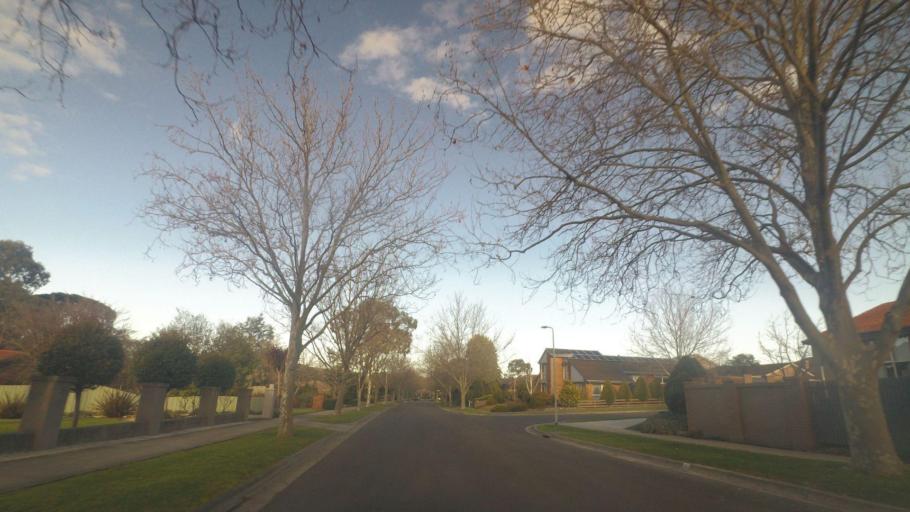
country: AU
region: Victoria
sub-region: Knox
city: Scoresby
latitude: -37.9143
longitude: 145.2381
